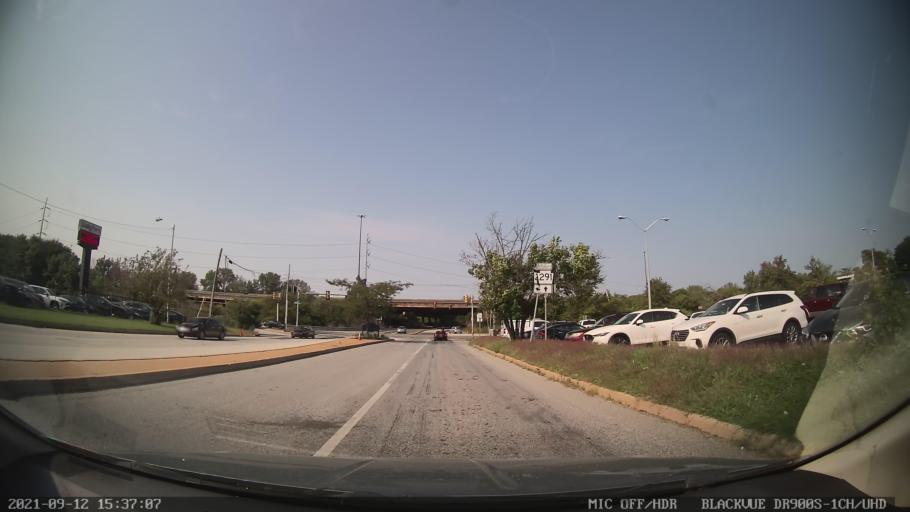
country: US
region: Pennsylvania
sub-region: Delaware County
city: Folcroft
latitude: 39.8746
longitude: -75.2618
